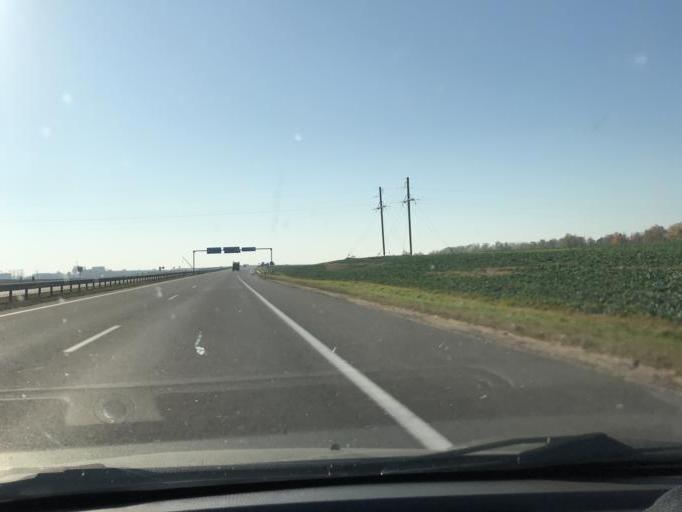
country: BY
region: Minsk
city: Pryvol'ny
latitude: 53.8093
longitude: 27.8052
